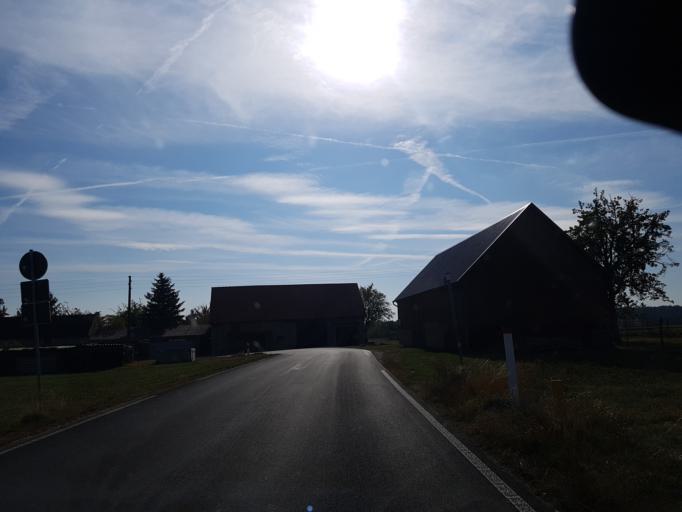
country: DE
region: Brandenburg
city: Schonborn
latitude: 51.6718
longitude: 13.4721
